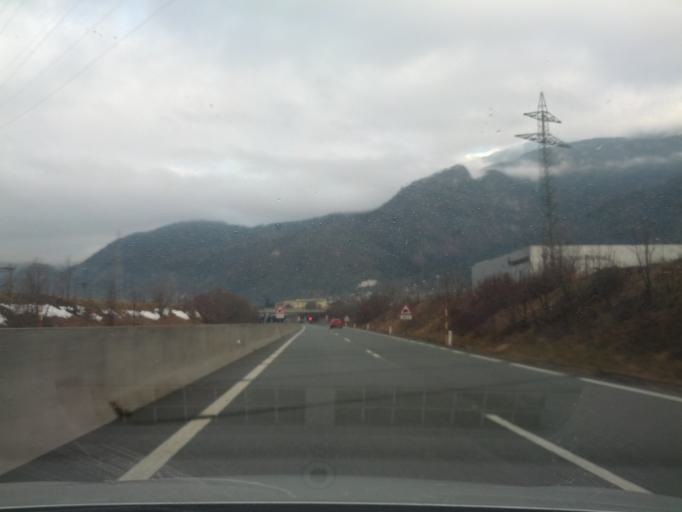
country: SI
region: Zirovnica
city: Zirovnica
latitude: 46.4005
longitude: 14.1313
